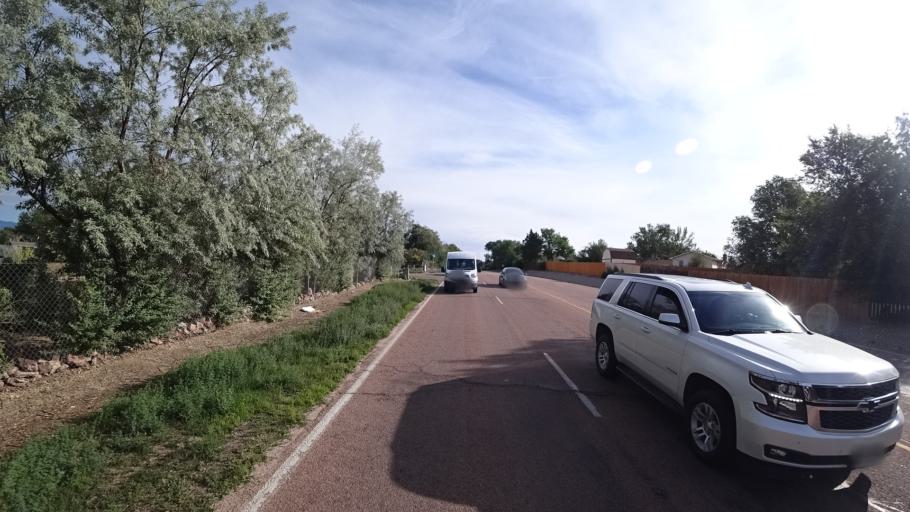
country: US
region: Colorado
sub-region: El Paso County
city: Security-Widefield
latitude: 38.7286
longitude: -104.6976
